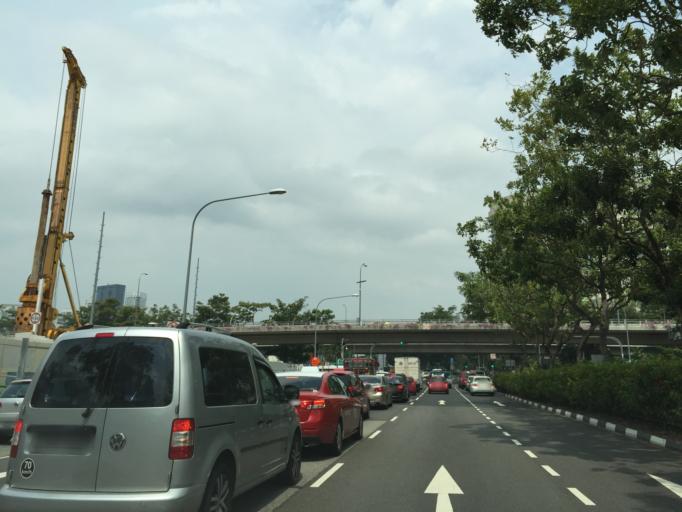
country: SG
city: Singapore
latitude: 1.3218
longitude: 103.8259
